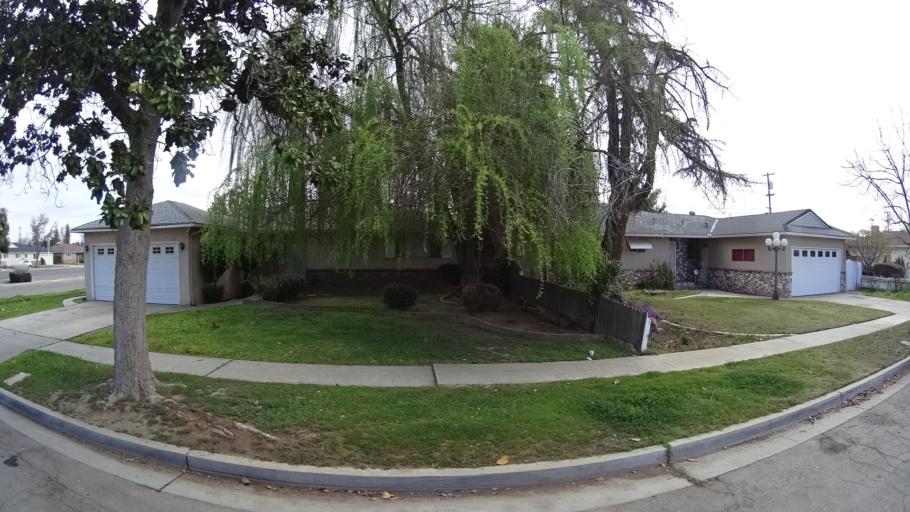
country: US
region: California
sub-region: Fresno County
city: Fresno
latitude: 36.8154
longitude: -119.7750
